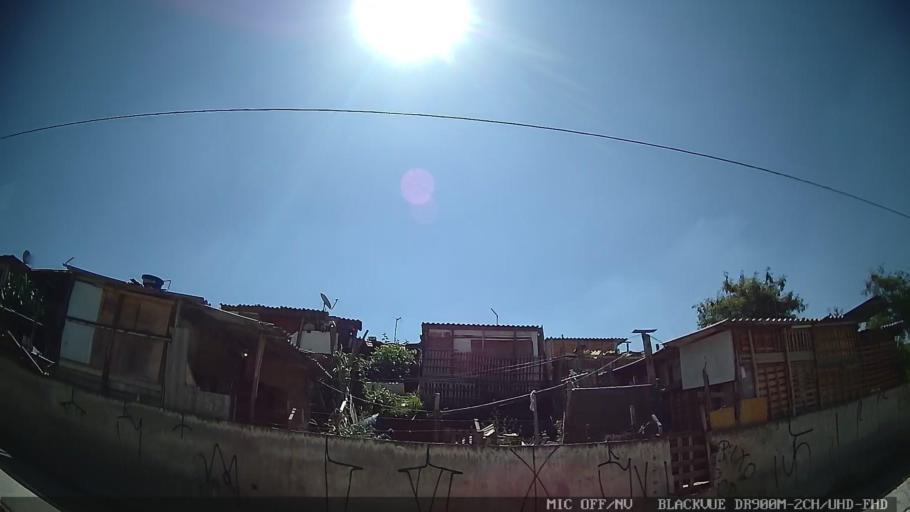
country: BR
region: Sao Paulo
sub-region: Sao Caetano Do Sul
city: Sao Caetano do Sul
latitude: -23.5865
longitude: -46.5052
